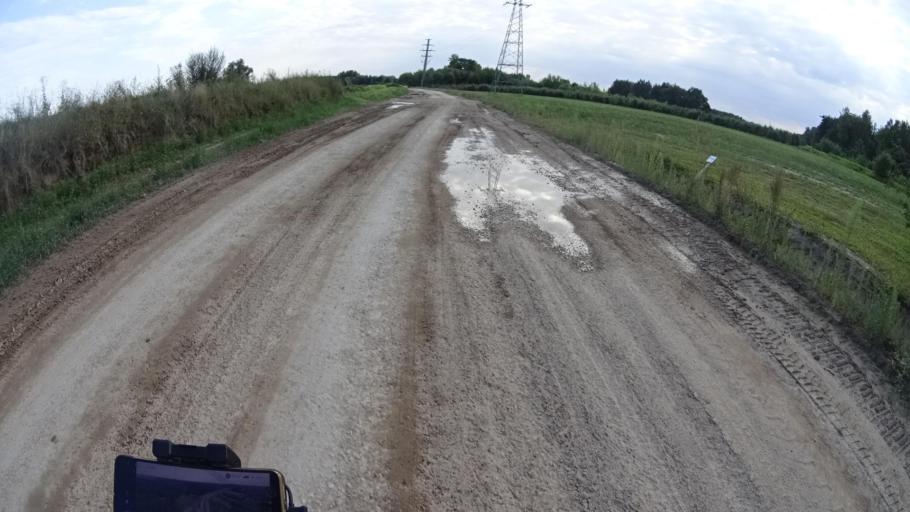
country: PL
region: Masovian Voivodeship
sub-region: Powiat piaseczynski
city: Tarczyn
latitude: 51.9846
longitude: 20.8697
